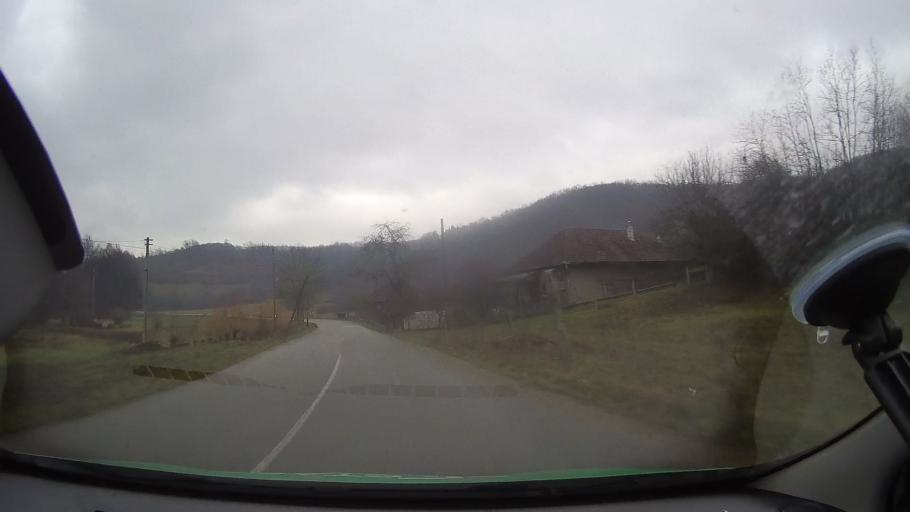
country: RO
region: Hunedoara
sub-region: Comuna Tomesti
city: Tomesti
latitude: 46.1985
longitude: 22.6516
